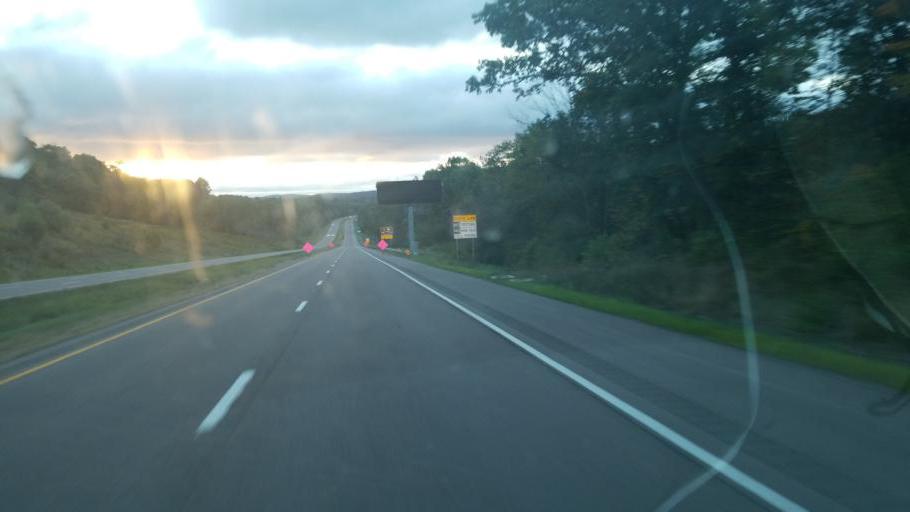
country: US
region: West Virginia
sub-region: Preston County
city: Terra Alta
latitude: 39.6603
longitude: -79.4619
